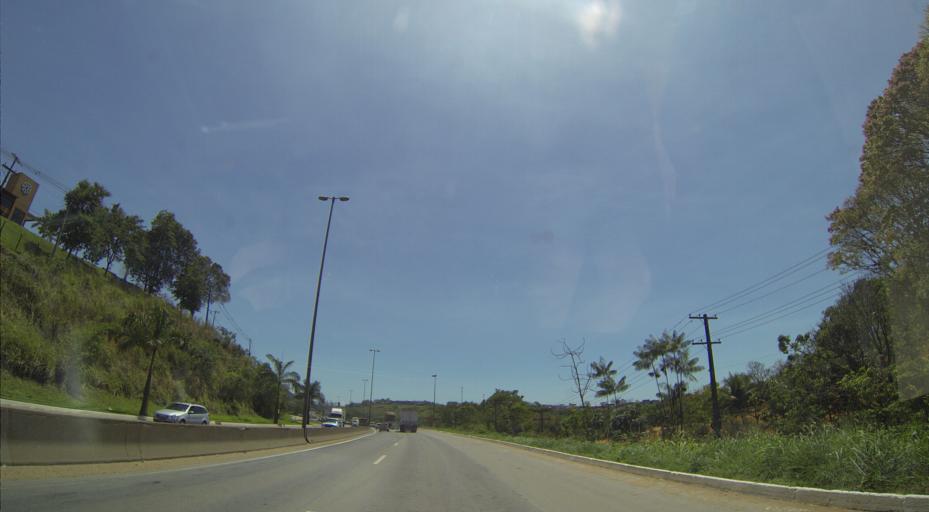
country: BR
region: Espirito Santo
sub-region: Vitoria
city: Vitoria
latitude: -20.3520
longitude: -40.4139
